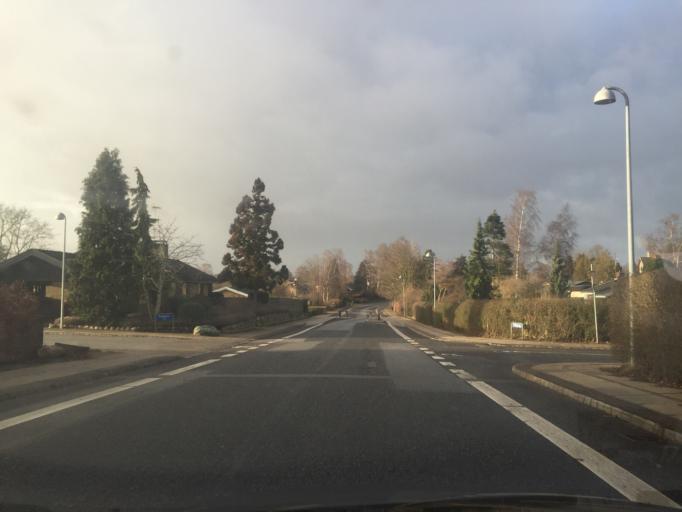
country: DK
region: Capital Region
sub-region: Herlev Kommune
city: Herlev
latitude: 55.7554
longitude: 12.4082
